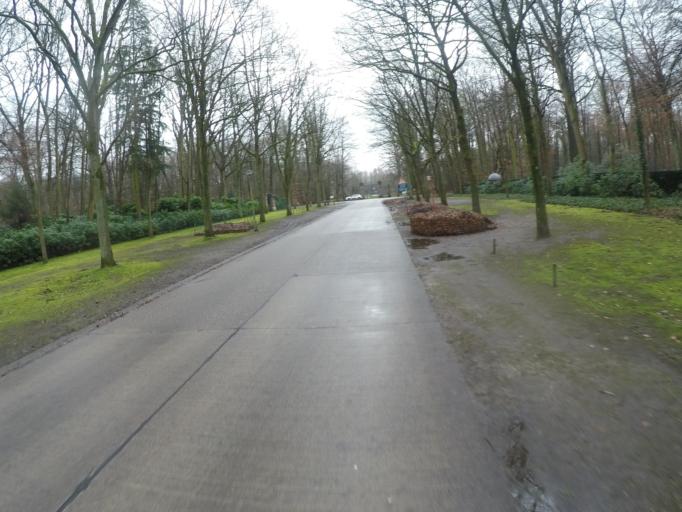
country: BE
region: Flanders
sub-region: Provincie Antwerpen
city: Schilde
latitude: 51.2253
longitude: 4.5696
